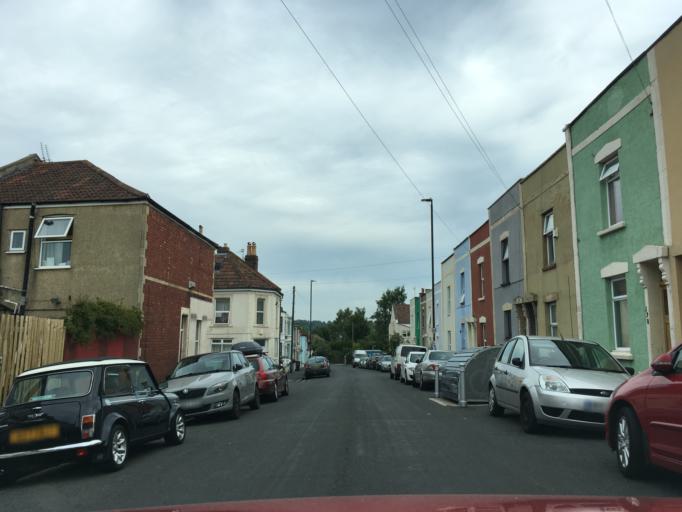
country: GB
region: England
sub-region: Bristol
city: Bristol
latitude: 51.4657
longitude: -2.5579
